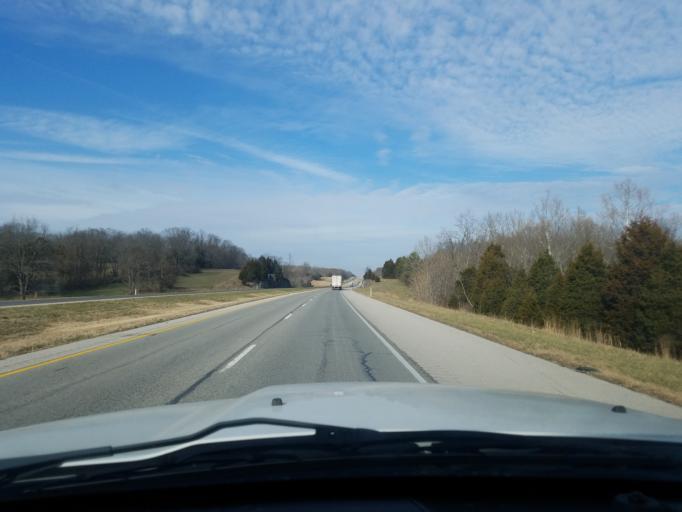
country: US
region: Indiana
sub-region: Monroe County
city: Bloomington
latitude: 39.0392
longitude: -86.5358
